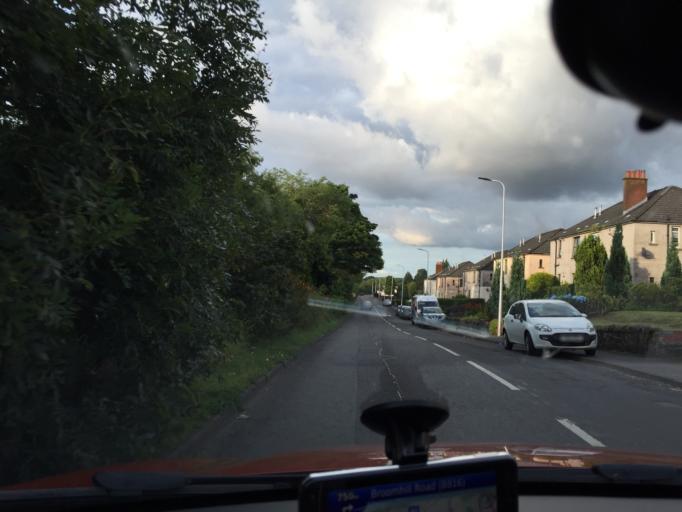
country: GB
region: Scotland
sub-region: Falkirk
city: Bonnybridge
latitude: 55.9950
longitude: -3.8958
